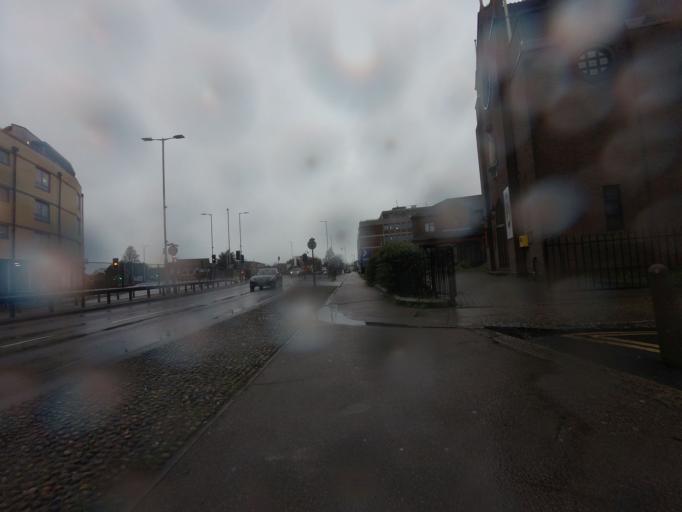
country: GB
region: England
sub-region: Hertfordshire
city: Waltham Cross
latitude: 51.6887
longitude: -0.0331
